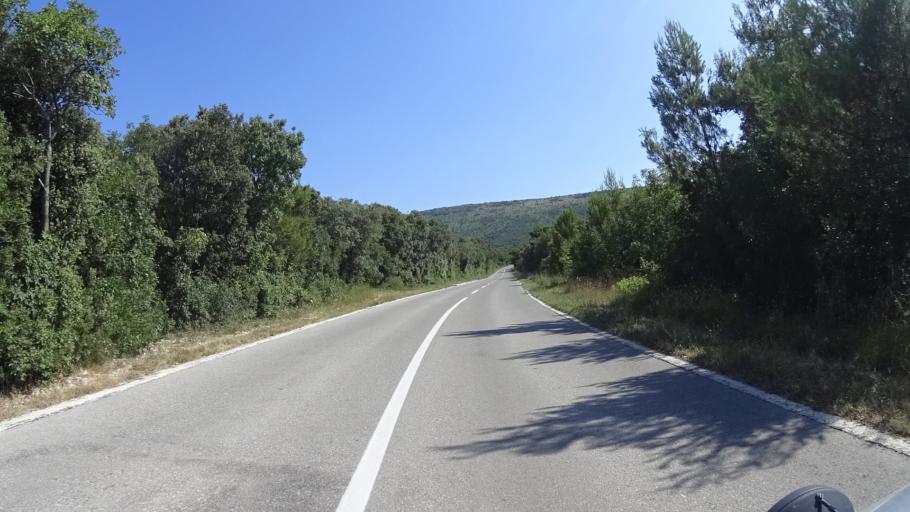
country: HR
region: Istarska
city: Rasa
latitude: 44.9772
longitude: 14.1061
